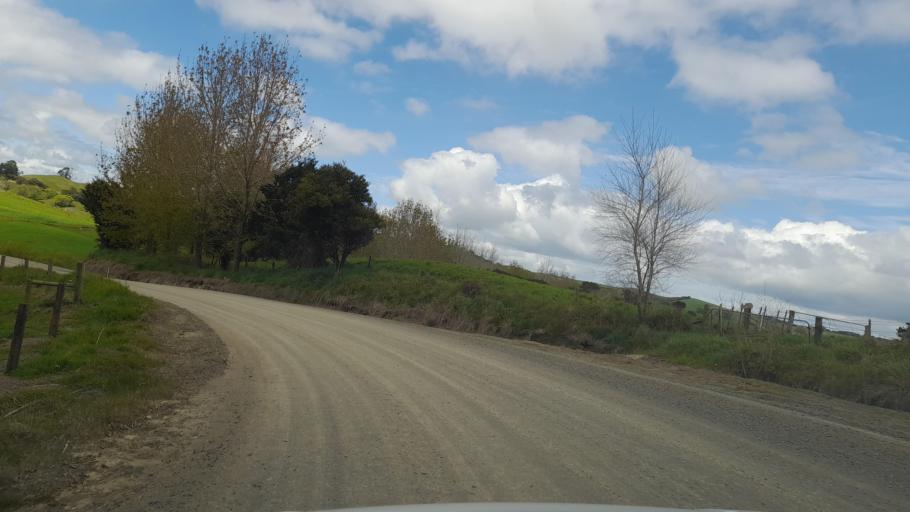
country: NZ
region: Auckland
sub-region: Auckland
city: Wellsford
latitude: -36.1729
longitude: 174.3171
